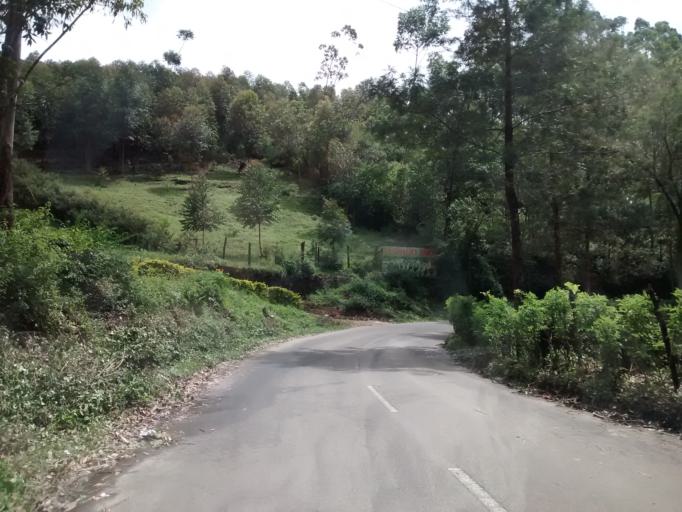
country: IN
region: Kerala
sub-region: Idukki
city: Munnar
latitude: 10.0943
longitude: 77.0977
